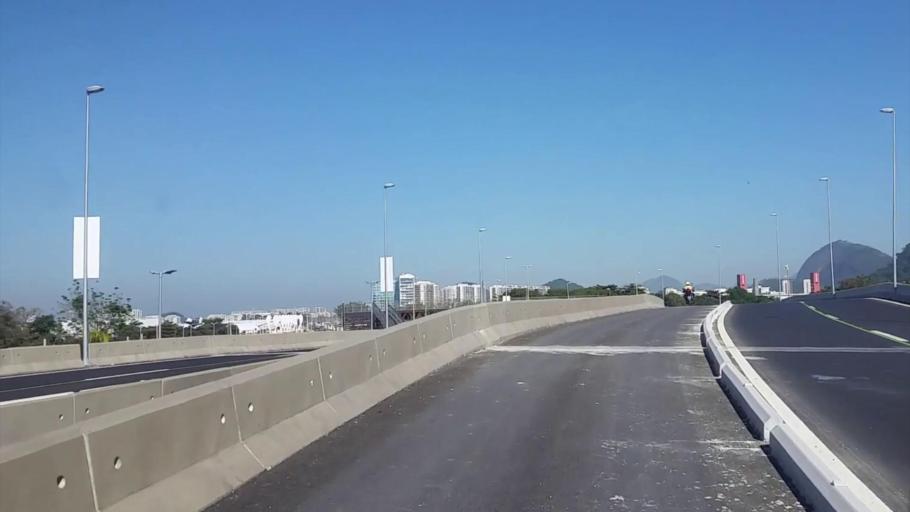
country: BR
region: Rio de Janeiro
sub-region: Nilopolis
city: Nilopolis
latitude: -22.9659
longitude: -43.3964
